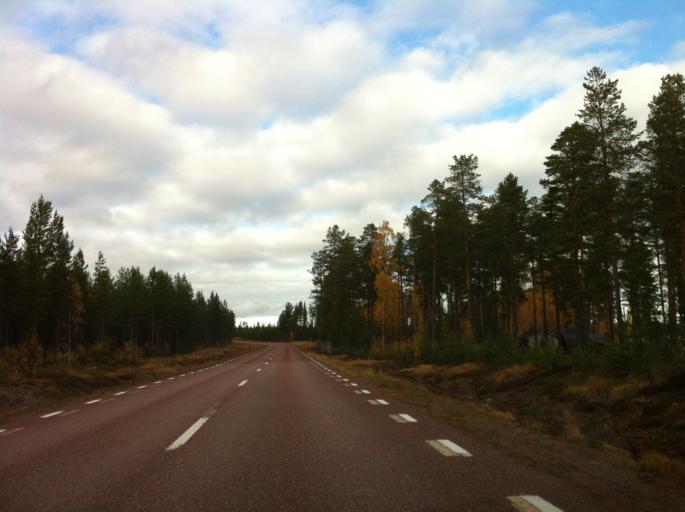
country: SE
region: Dalarna
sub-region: Alvdalens Kommun
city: AElvdalen
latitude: 61.5445
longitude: 13.3373
